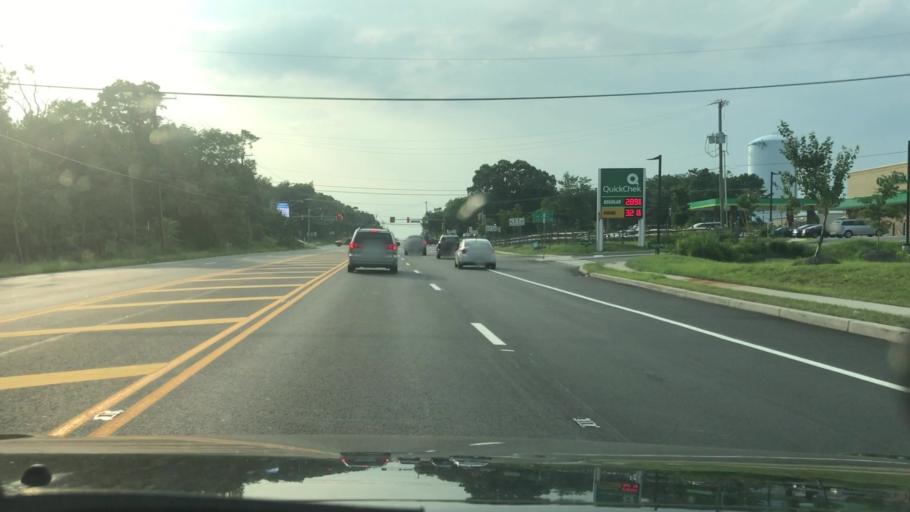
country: US
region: New Jersey
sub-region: Ocean County
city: Leisure Village
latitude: 40.0751
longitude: -74.1826
